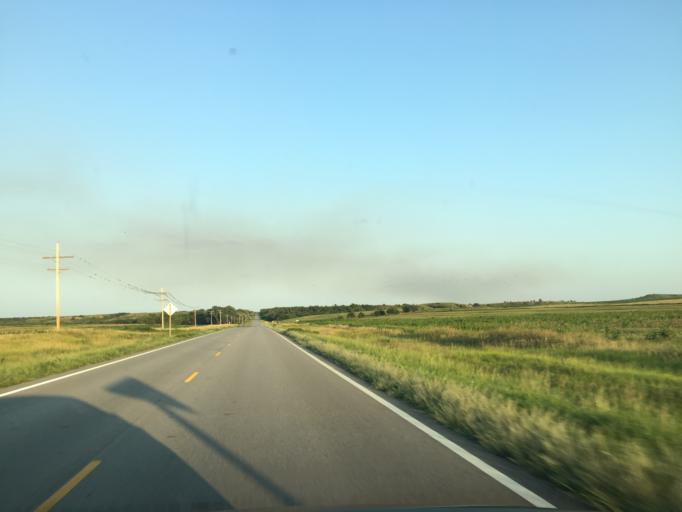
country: US
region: Kansas
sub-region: Ellsworth County
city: Ellsworth
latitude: 38.7087
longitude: -98.2304
